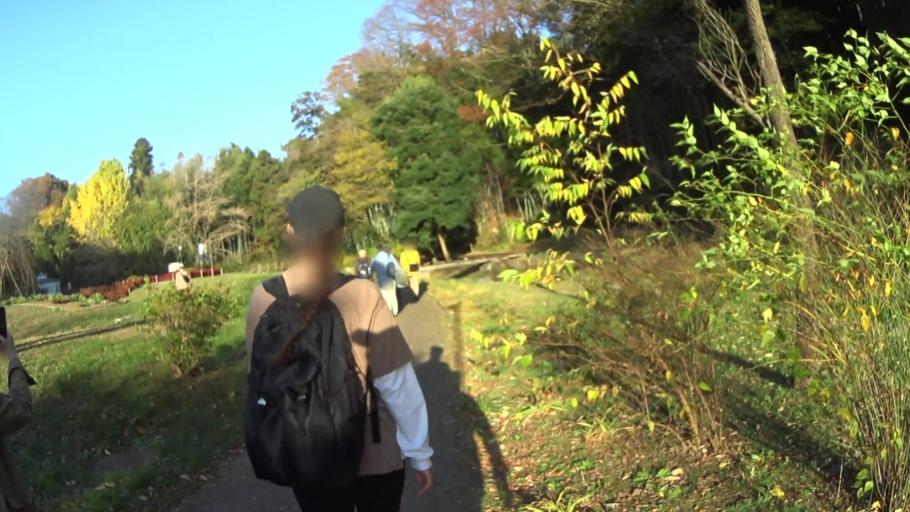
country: JP
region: Ibaraki
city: Mito-shi
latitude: 36.3757
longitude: 140.4618
